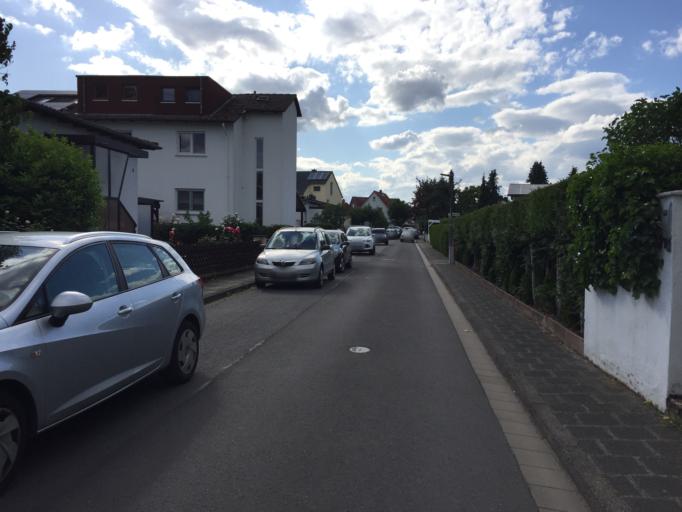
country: DE
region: Hesse
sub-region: Regierungsbezirk Darmstadt
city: Karben
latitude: 50.2462
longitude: 8.7549
